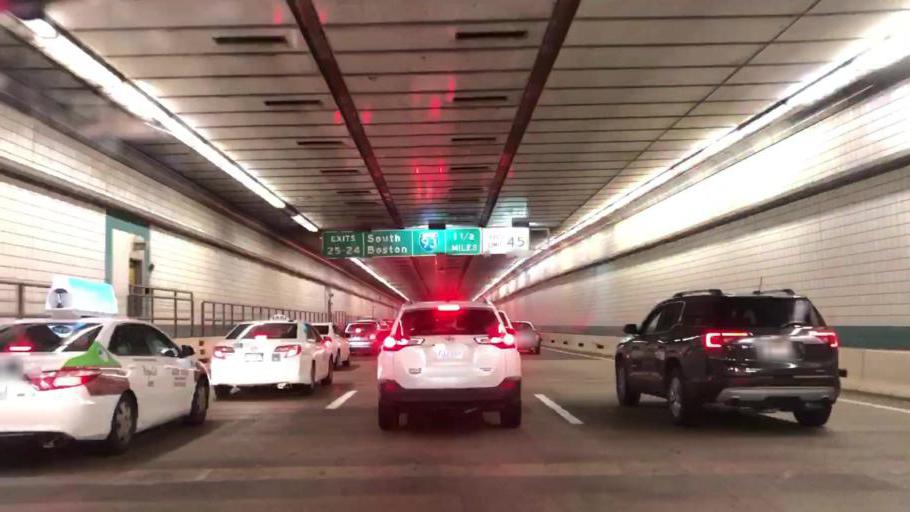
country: US
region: Massachusetts
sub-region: Suffolk County
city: Chelsea
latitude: 42.3623
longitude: -71.0246
